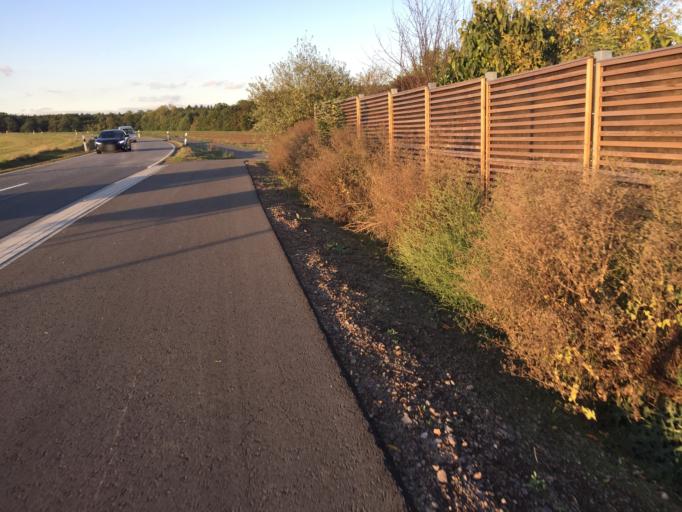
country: DE
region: Hesse
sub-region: Regierungsbezirk Darmstadt
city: Munzenberg
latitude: 50.5071
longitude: 8.7581
